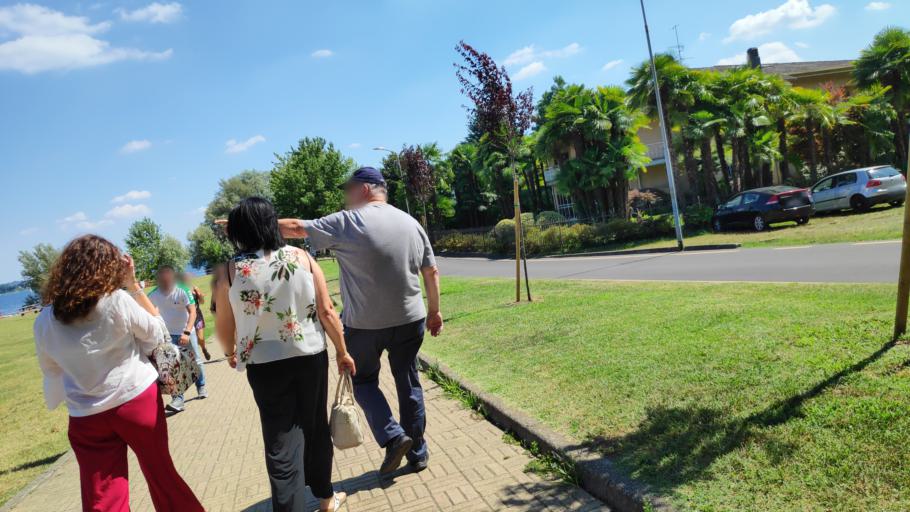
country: IT
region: Piedmont
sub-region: Provincia di Novara
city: Arona
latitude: 45.7536
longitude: 8.5667
